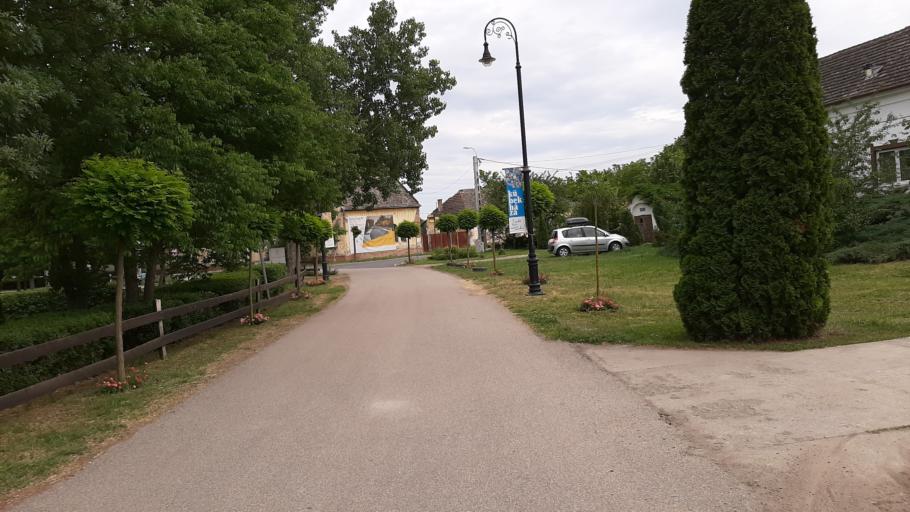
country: RO
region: Timis
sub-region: Comuna Beba Veche
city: Beba Veche
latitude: 46.1492
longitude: 20.2755
